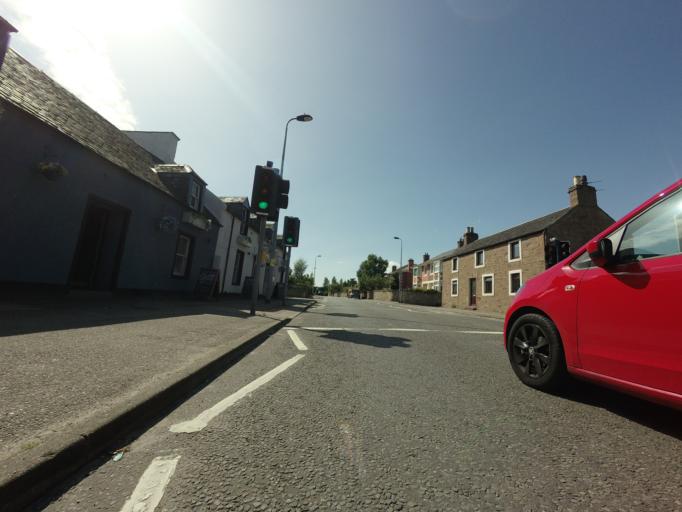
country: GB
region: Scotland
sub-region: Highland
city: Inverness
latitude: 57.4731
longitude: -4.1995
